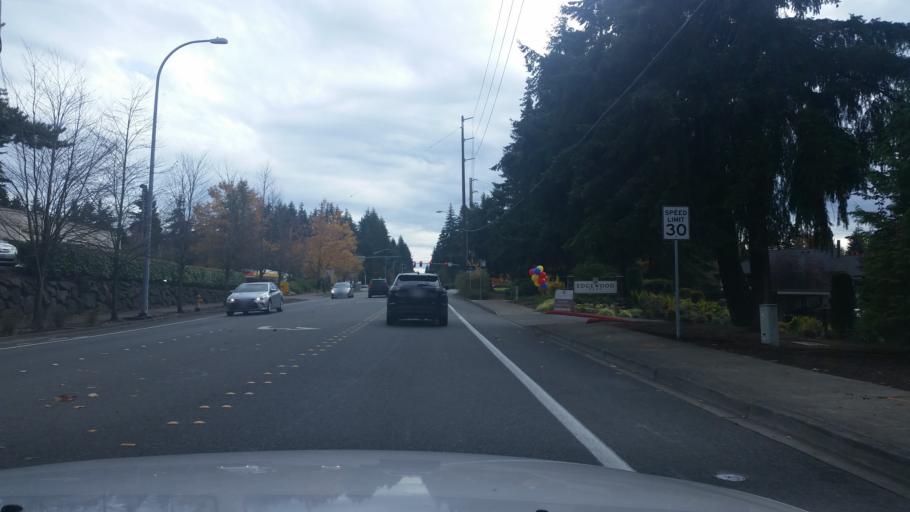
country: US
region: Washington
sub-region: King County
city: Eastgate
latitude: 47.5975
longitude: -122.1509
